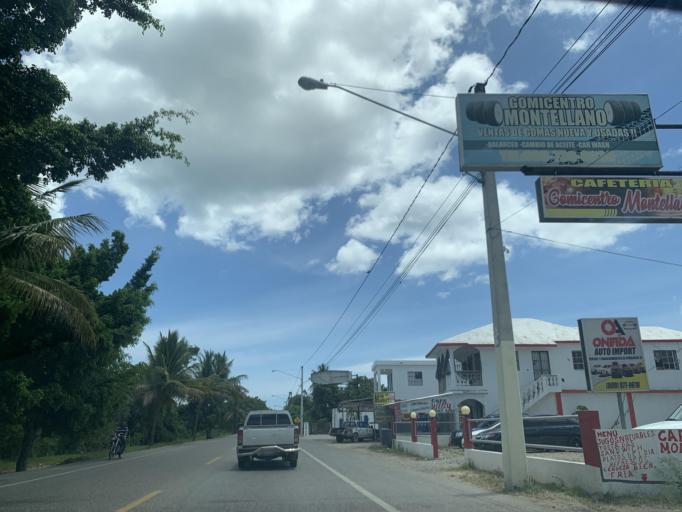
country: DO
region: Puerto Plata
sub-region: Puerto Plata
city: Puerto Plata
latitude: 19.7296
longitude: -70.6066
